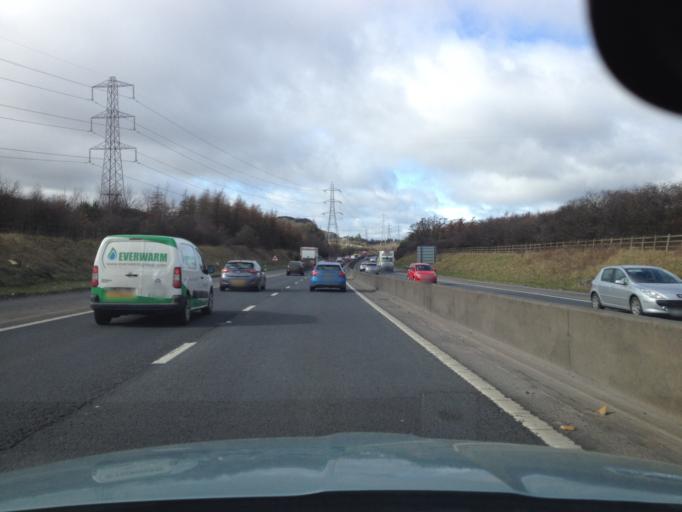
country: GB
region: Scotland
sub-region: Edinburgh
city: Colinton
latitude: 55.8985
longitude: -3.2478
